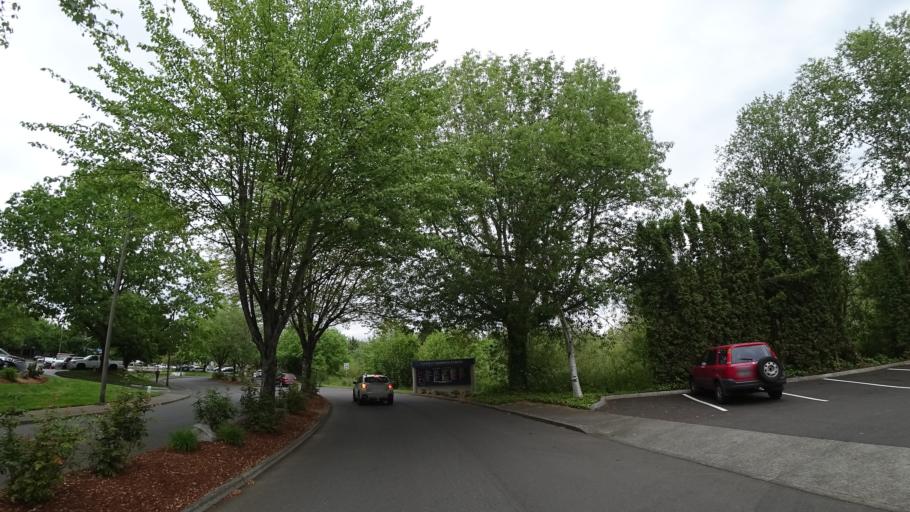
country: US
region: Oregon
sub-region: Washington County
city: Tigard
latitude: 45.4464
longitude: -122.7889
